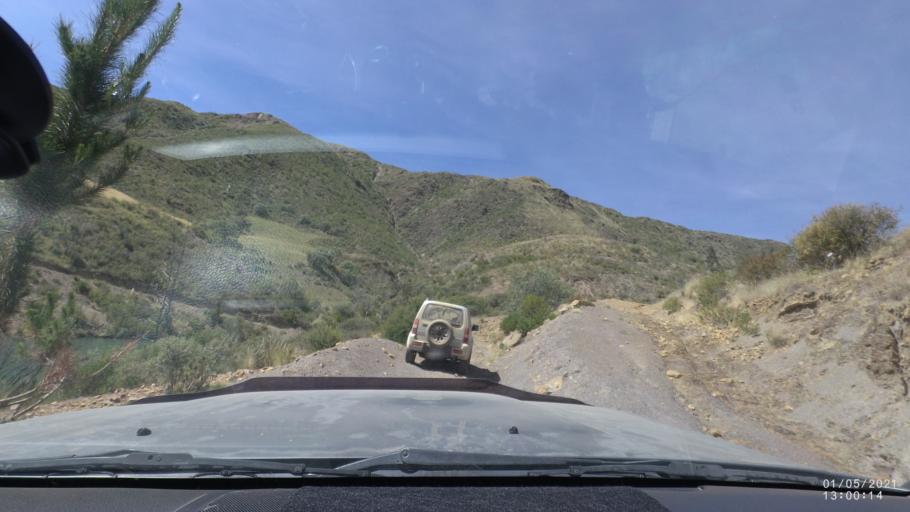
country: BO
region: Cochabamba
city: Capinota
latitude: -17.6837
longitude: -66.1653
